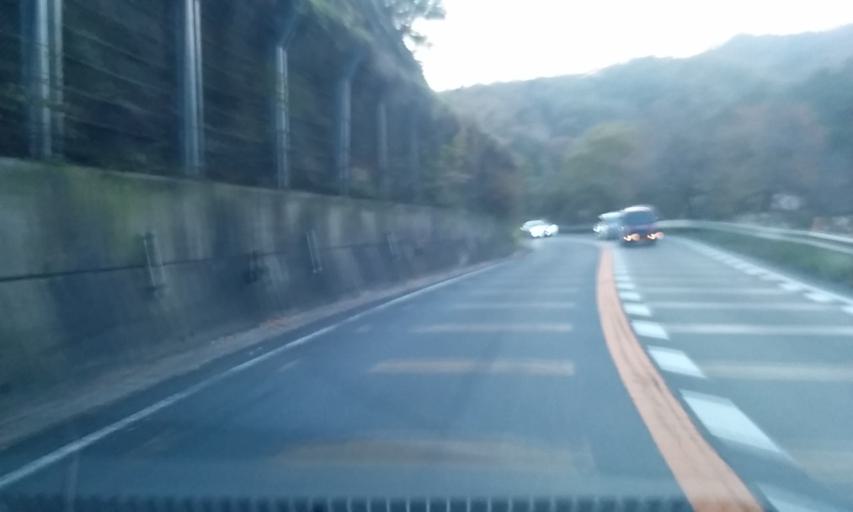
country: JP
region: Kyoto
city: Kameoka
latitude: 35.1226
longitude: 135.4521
